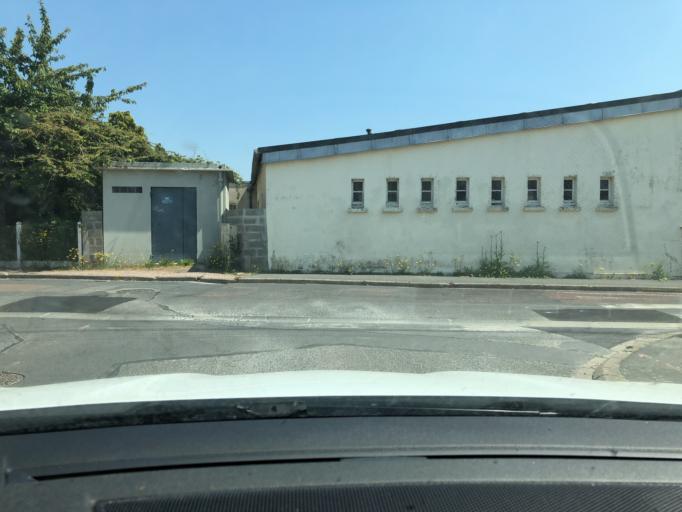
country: FR
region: Lower Normandy
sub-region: Departement du Calvados
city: Lion-sur-Mer
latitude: 49.3016
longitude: -0.3229
